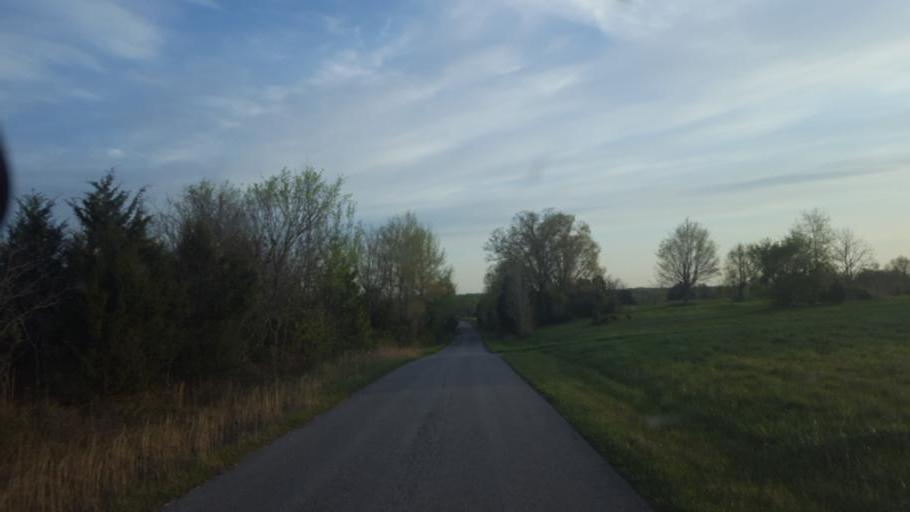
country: US
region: Kentucky
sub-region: Barren County
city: Cave City
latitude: 37.1664
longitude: -86.0079
